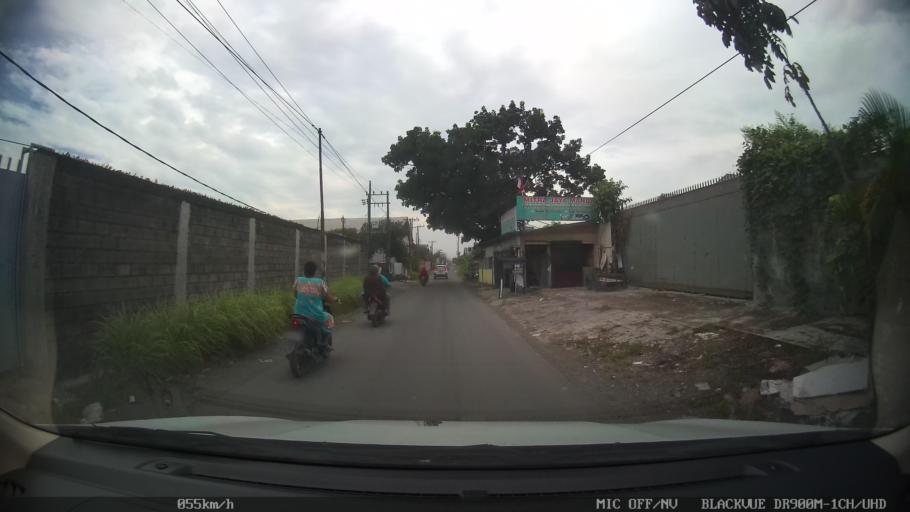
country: ID
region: North Sumatra
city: Sunggal
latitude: 3.6147
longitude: 98.5815
